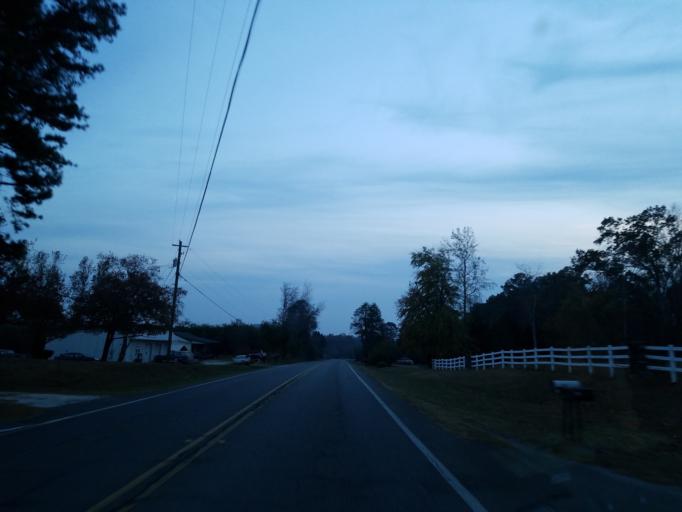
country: US
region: Georgia
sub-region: Pickens County
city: Jasper
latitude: 34.5085
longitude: -84.5590
